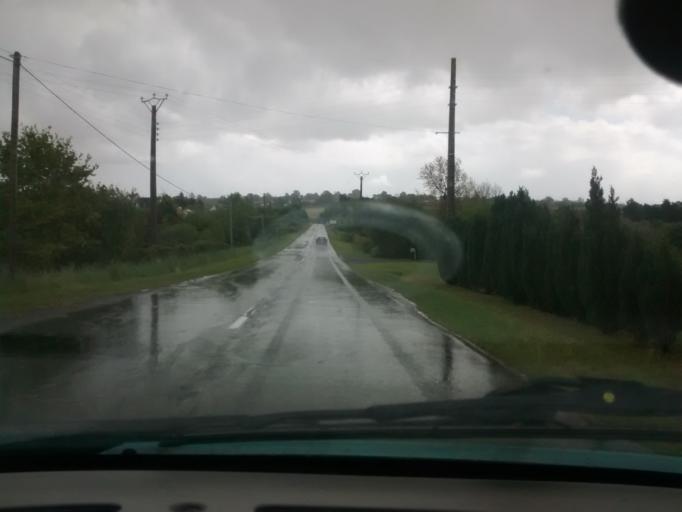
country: FR
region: Lower Normandy
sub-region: Departement de la Manche
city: Conde-sur-Vire
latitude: 49.0617
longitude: -1.0096
